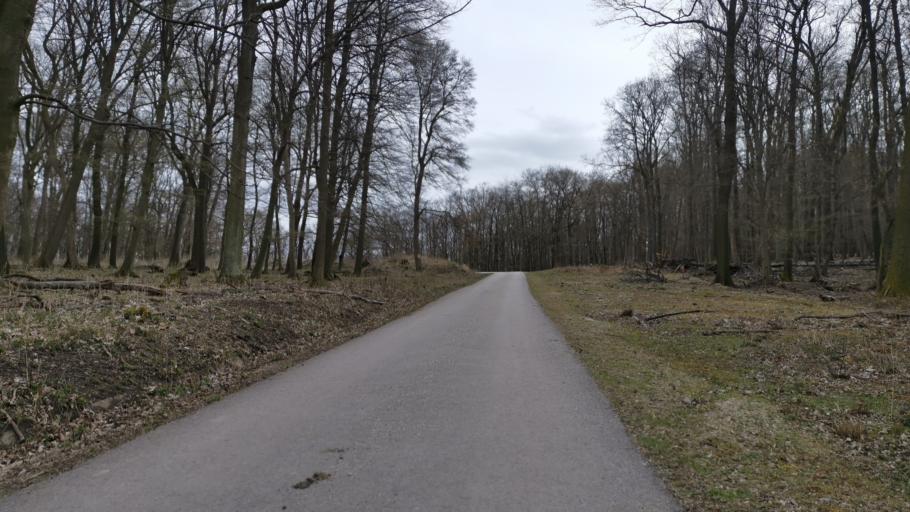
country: CZ
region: South Moravian
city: Petrov
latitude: 48.8076
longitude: 17.3260
